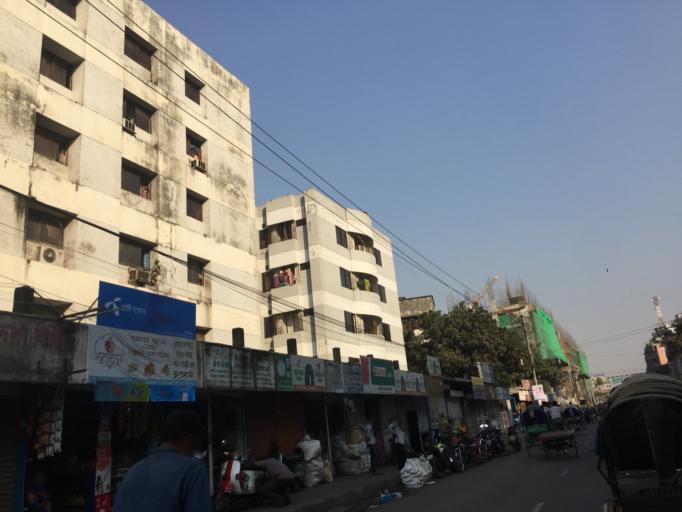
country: BD
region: Dhaka
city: Azimpur
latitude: 23.7241
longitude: 90.3990
